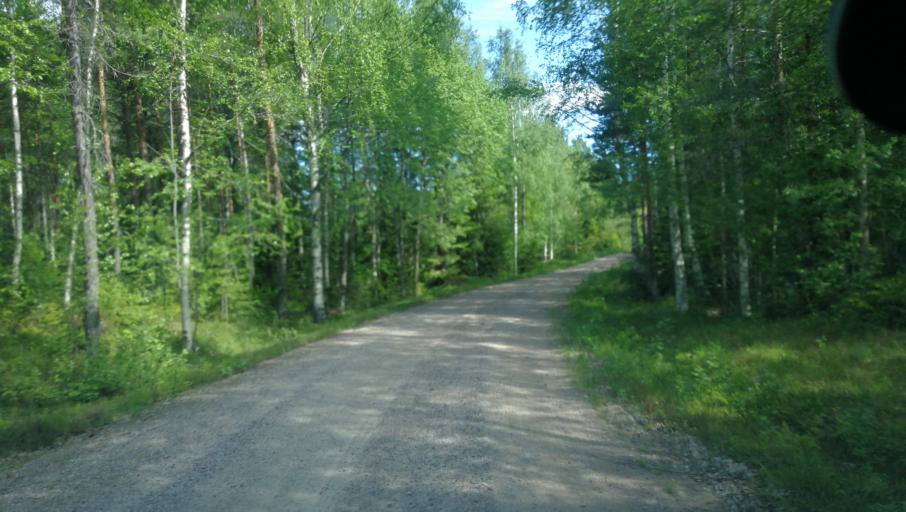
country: SE
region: Dalarna
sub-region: Vansbro Kommun
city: Vansbro
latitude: 60.8244
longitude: 14.1662
